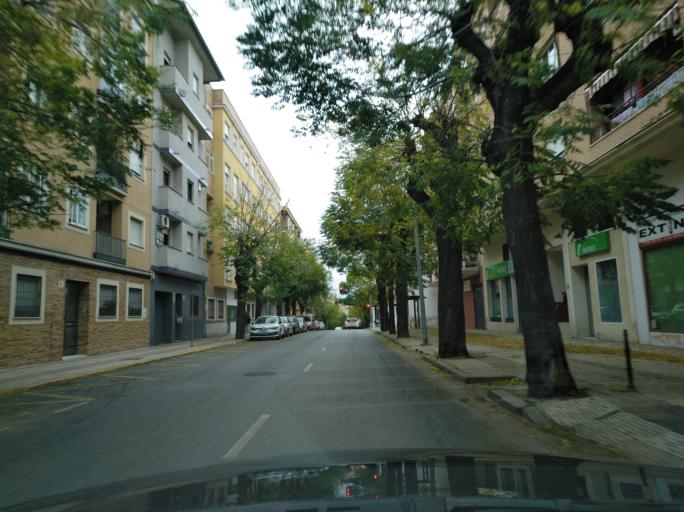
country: ES
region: Extremadura
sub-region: Provincia de Badajoz
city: Badajoz
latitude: 38.8879
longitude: -6.9777
